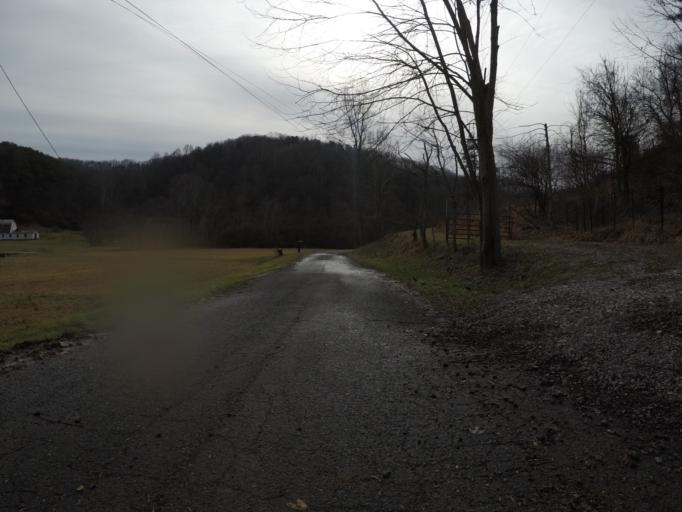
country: US
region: West Virginia
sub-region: Wayne County
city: Lavalette
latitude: 38.3264
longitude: -82.3773
